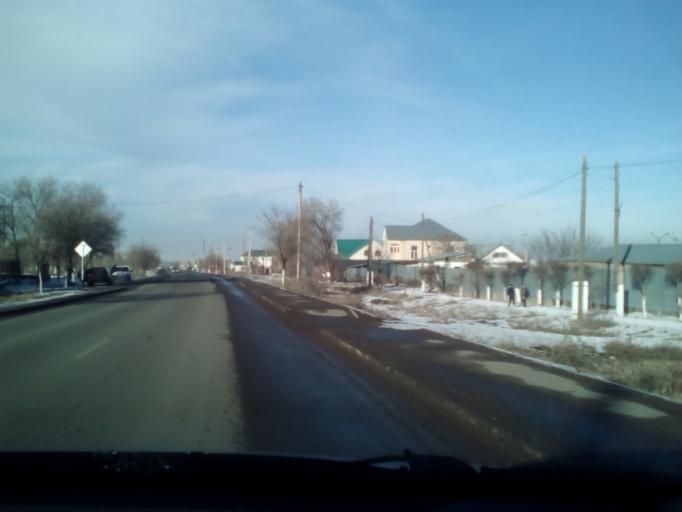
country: KZ
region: Almaty Oblysy
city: Burunday
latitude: 43.1859
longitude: 76.4147
